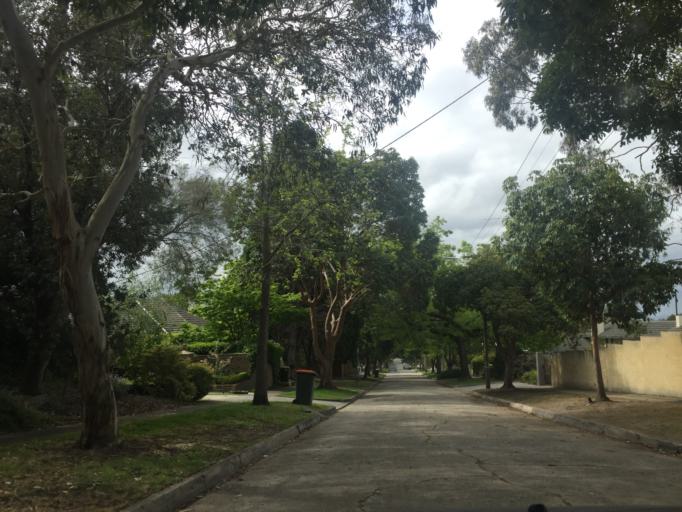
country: AU
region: Victoria
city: Balwyn
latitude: -37.8154
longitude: 145.0664
